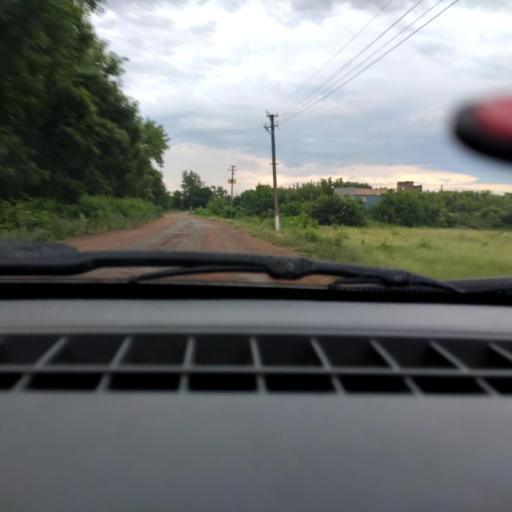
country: RU
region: Bashkortostan
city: Blagoveshchensk
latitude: 54.9282
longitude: 55.9682
